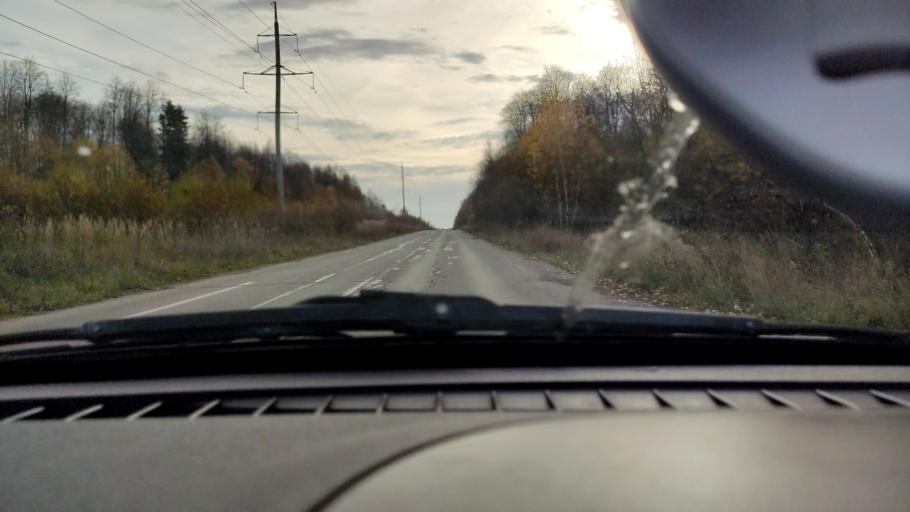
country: RU
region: Perm
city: Perm
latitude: 58.0929
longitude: 56.4075
